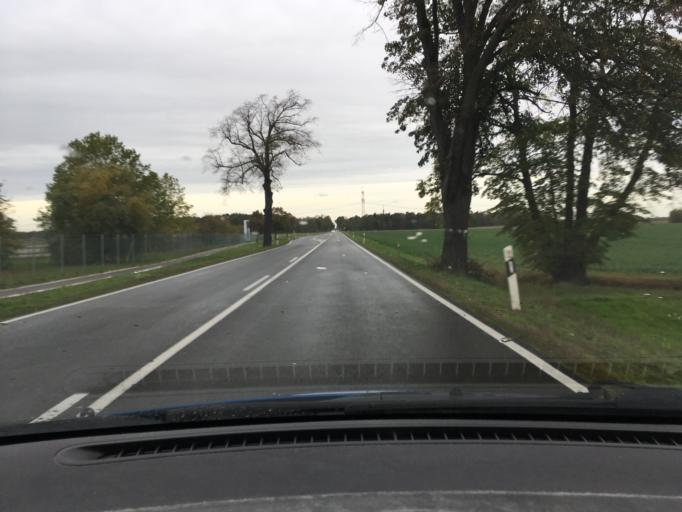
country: DE
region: Saxony-Anhalt
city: Zerbst
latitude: 51.9385
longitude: 12.1228
